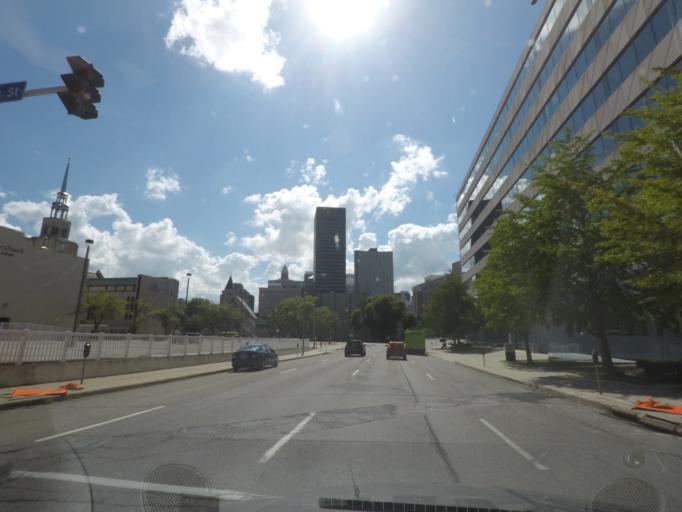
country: US
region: Iowa
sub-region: Polk County
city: Des Moines
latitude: 41.5905
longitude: -93.6269
